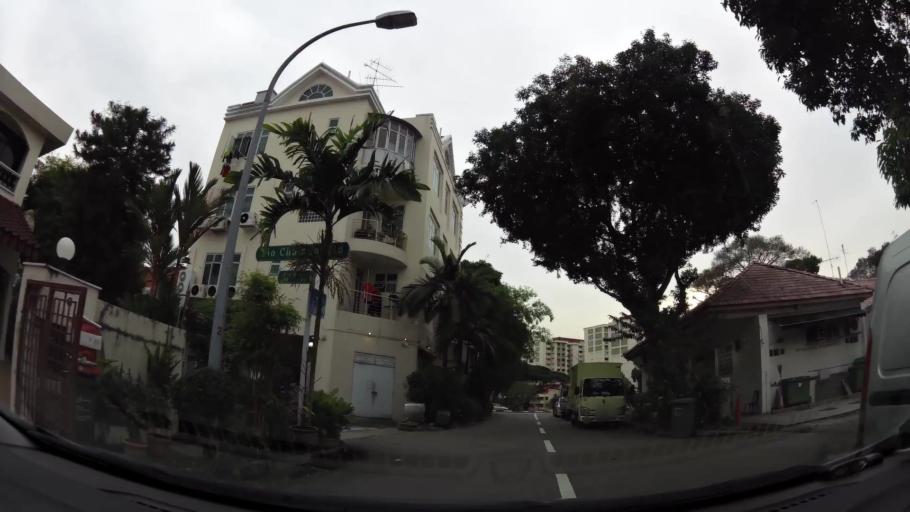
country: SG
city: Singapore
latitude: 1.3586
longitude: 103.8749
